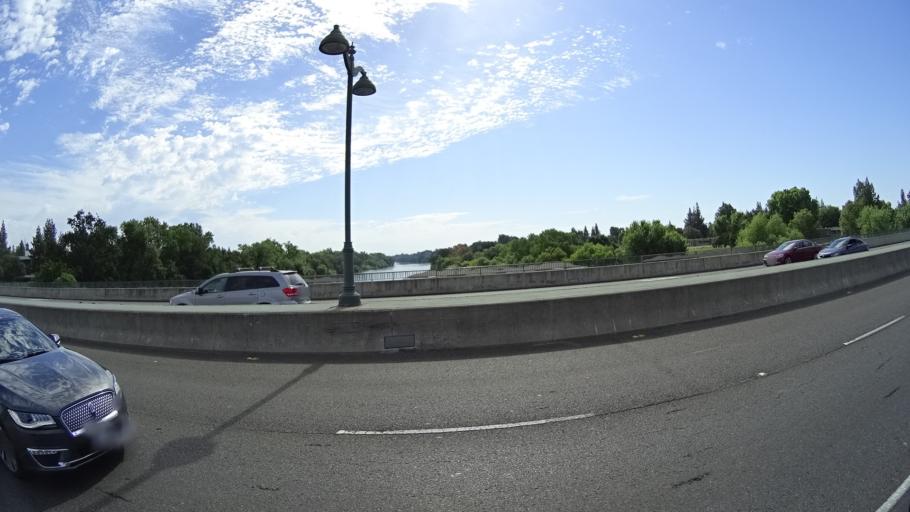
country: US
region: California
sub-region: Sacramento County
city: Rosemont
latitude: 38.5667
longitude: -121.3830
